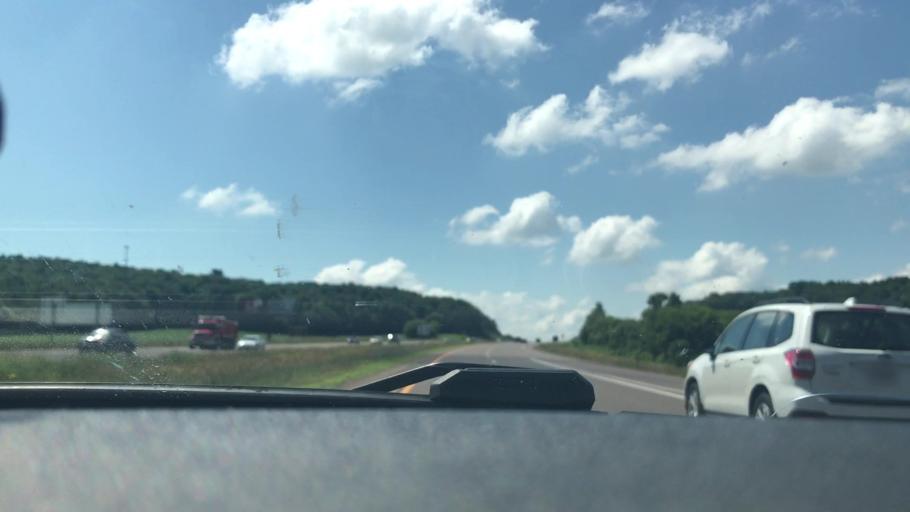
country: US
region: Wisconsin
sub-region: Chippewa County
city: Chippewa Falls
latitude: 44.9612
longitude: -91.4256
